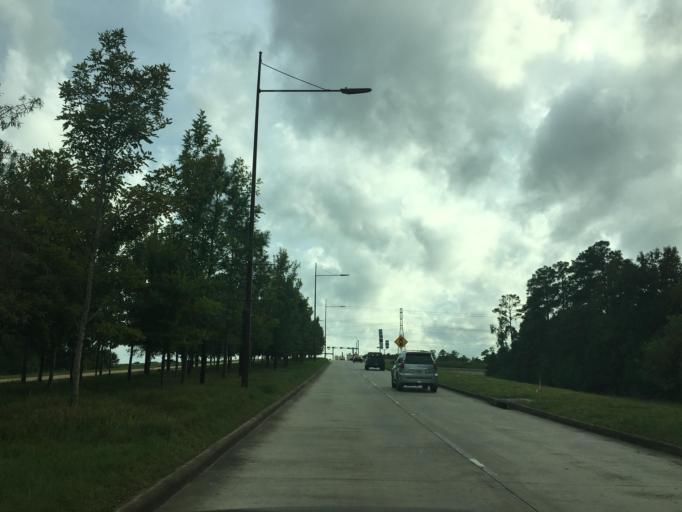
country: US
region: Texas
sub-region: Harris County
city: Spring
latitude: 30.0903
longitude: -95.4503
